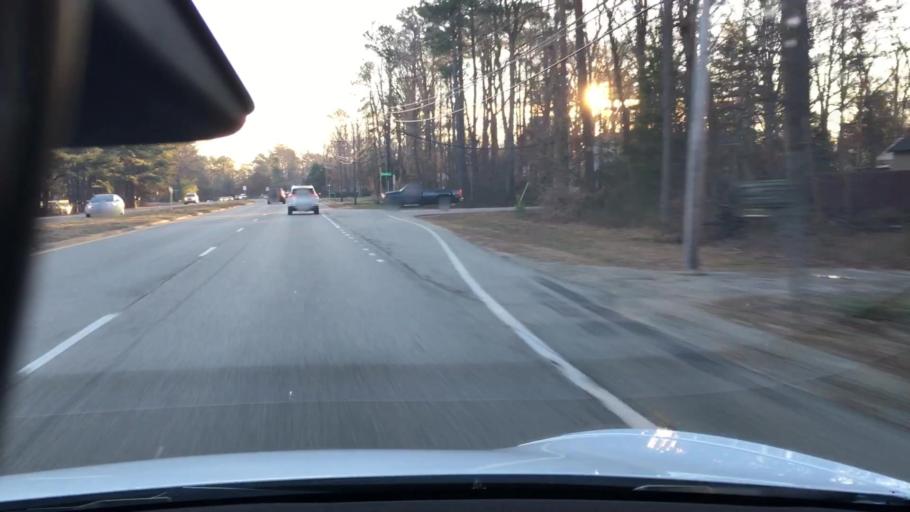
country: US
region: Virginia
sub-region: Chesterfield County
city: Bon Air
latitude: 37.5325
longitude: -77.5831
